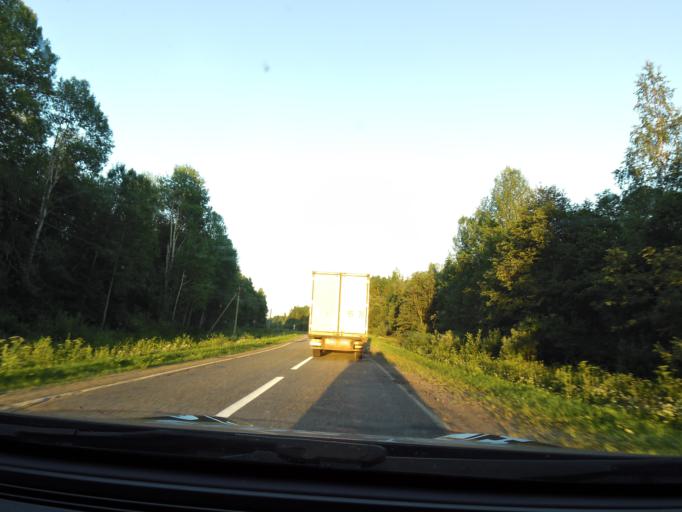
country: RU
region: Jaroslavl
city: Prechistoye
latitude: 58.4027
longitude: 40.3842
